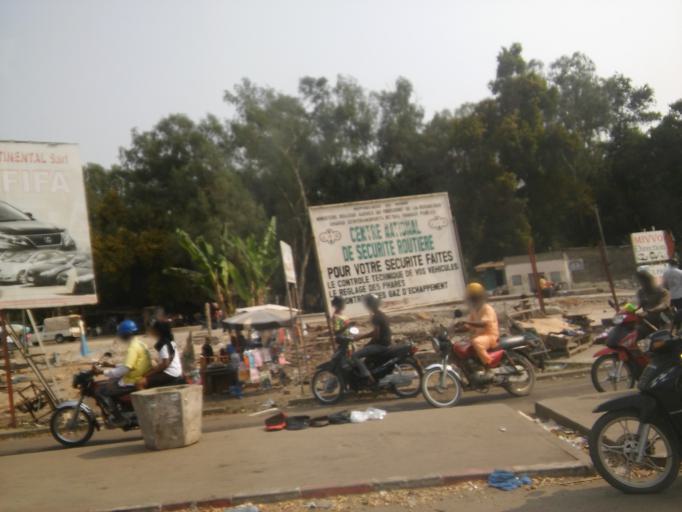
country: BJ
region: Littoral
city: Cotonou
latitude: 6.3727
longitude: 2.5460
